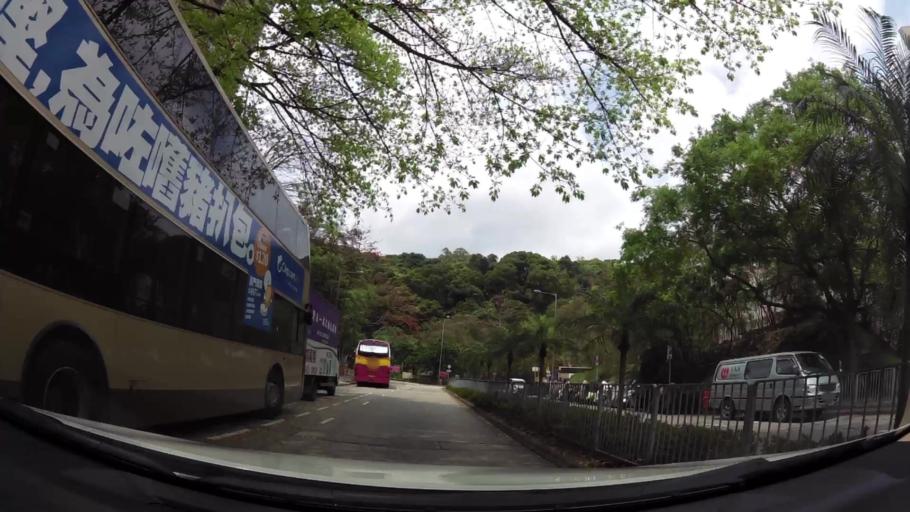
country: HK
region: Tuen Mun
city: Tuen Mun
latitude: 22.4010
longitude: 113.9666
